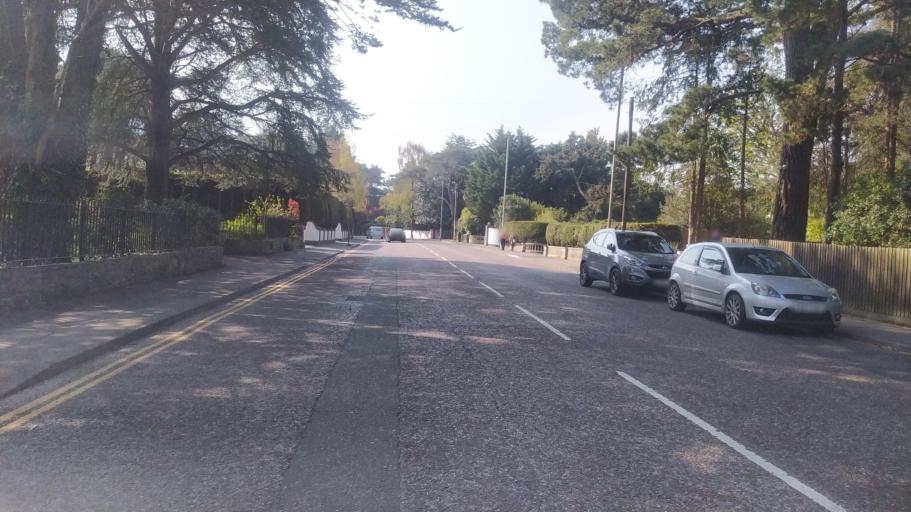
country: GB
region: England
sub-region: Dorset
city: Parkstone
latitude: 50.7100
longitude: -1.9262
